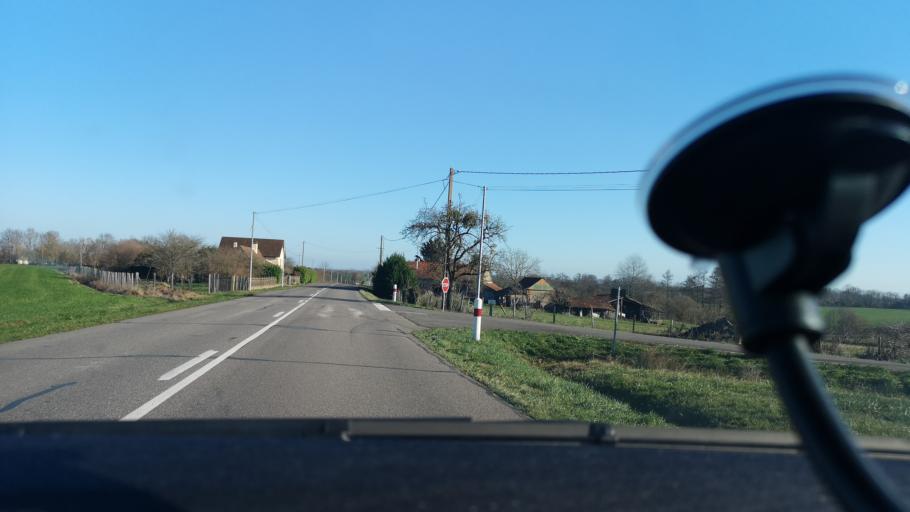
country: FR
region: Bourgogne
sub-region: Departement de Saone-et-Loire
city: Mervans
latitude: 46.7471
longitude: 5.1559
